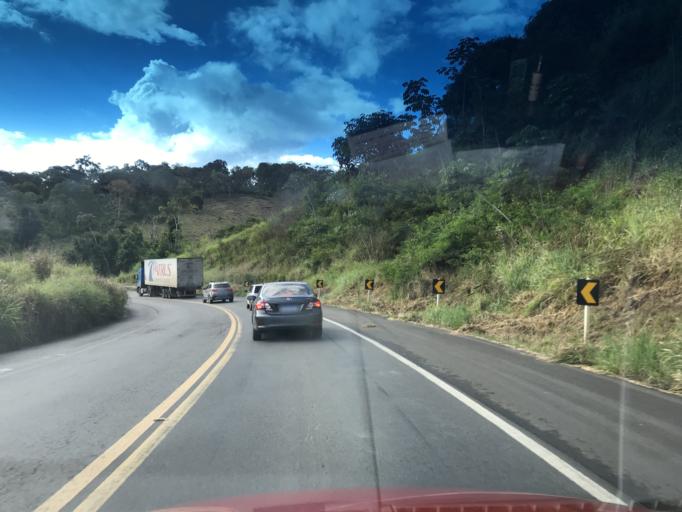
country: BR
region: Bahia
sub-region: Ibirapitanga
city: Ibirapitanga
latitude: -14.1727
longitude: -39.3233
